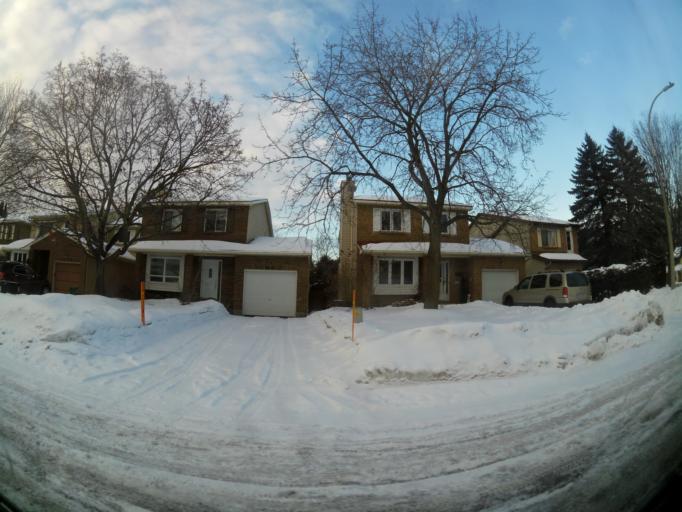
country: CA
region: Quebec
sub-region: Outaouais
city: Gatineau
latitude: 45.4563
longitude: -75.5426
